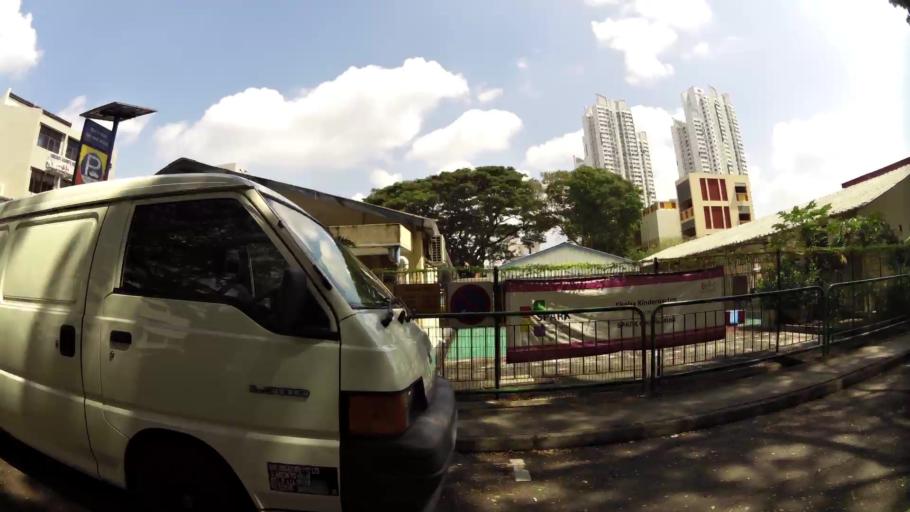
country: SG
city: Singapore
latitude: 1.3142
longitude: 103.8582
